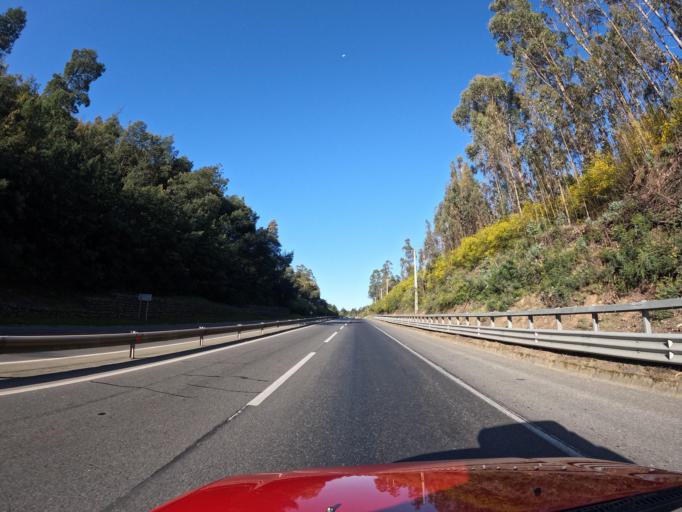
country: CL
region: Biobio
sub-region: Provincia de Concepcion
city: Penco
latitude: -36.7608
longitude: -72.9731
